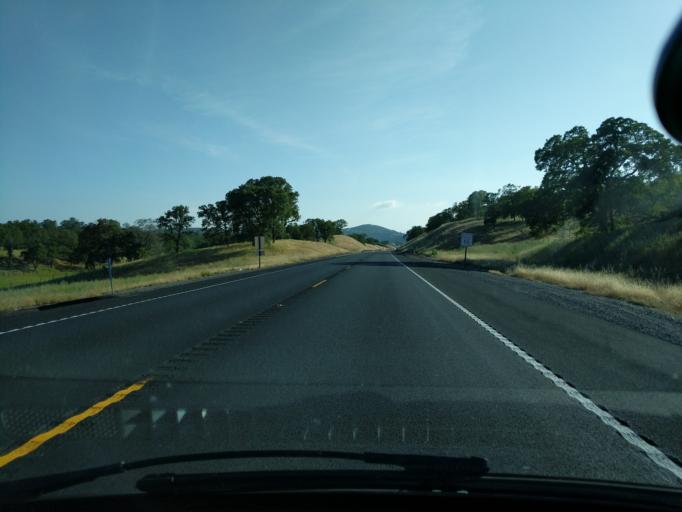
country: US
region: California
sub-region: Calaveras County
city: Copperopolis
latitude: 37.9702
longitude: -120.6595
